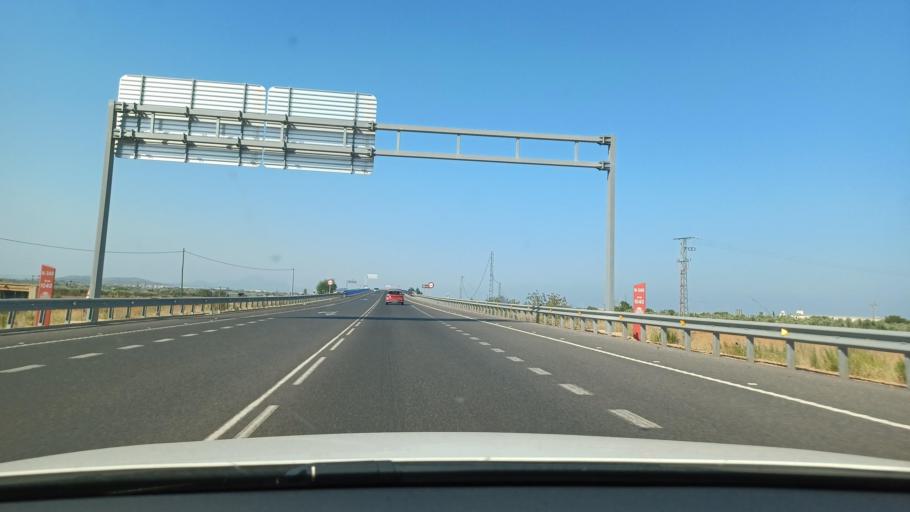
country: ES
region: Valencia
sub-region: Provincia de Castello
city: Benicarlo
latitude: 40.4061
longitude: 0.3773
